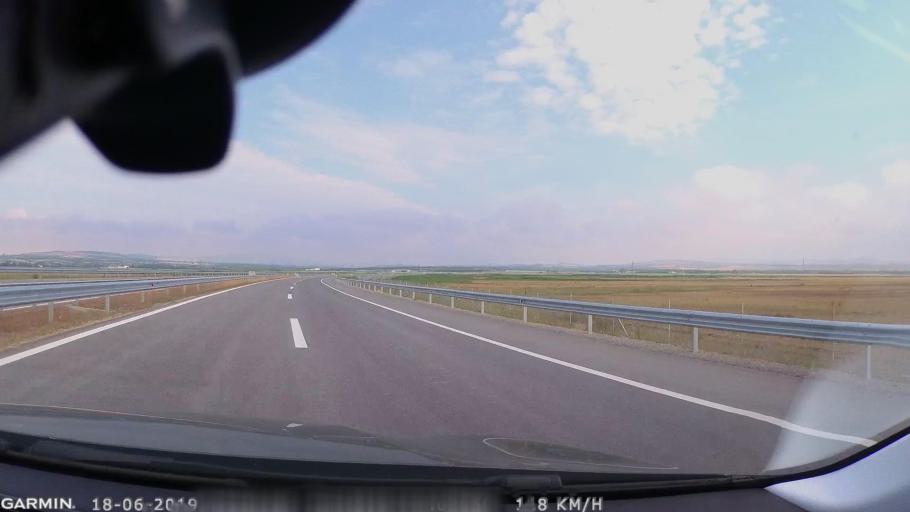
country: MK
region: Sveti Nikole
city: Sveti Nikole
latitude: 41.8153
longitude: 22.0200
